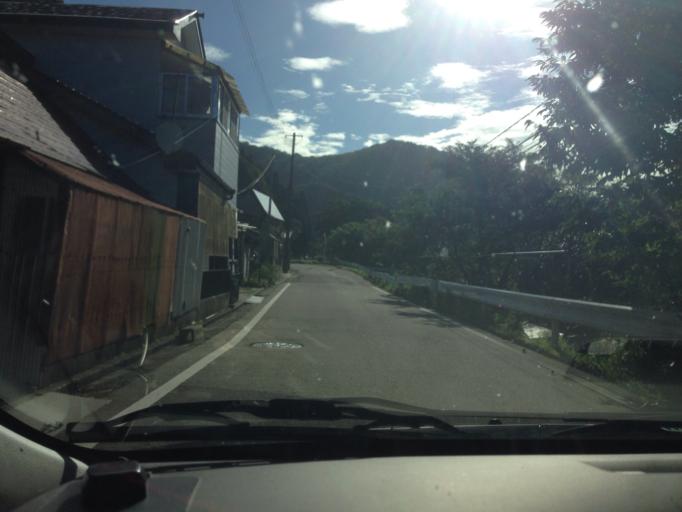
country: JP
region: Fukushima
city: Inawashiro
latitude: 37.4895
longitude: 140.1633
